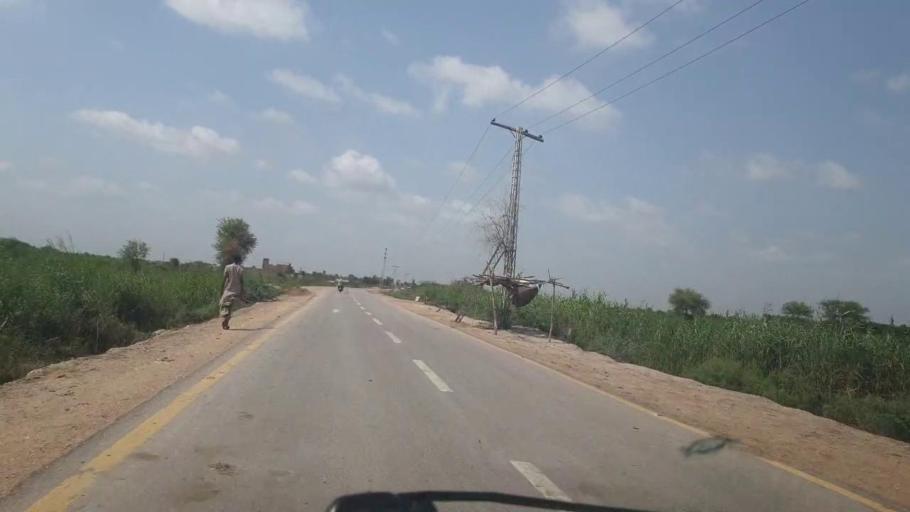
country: PK
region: Sindh
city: Berani
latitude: 25.6834
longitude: 68.9264
